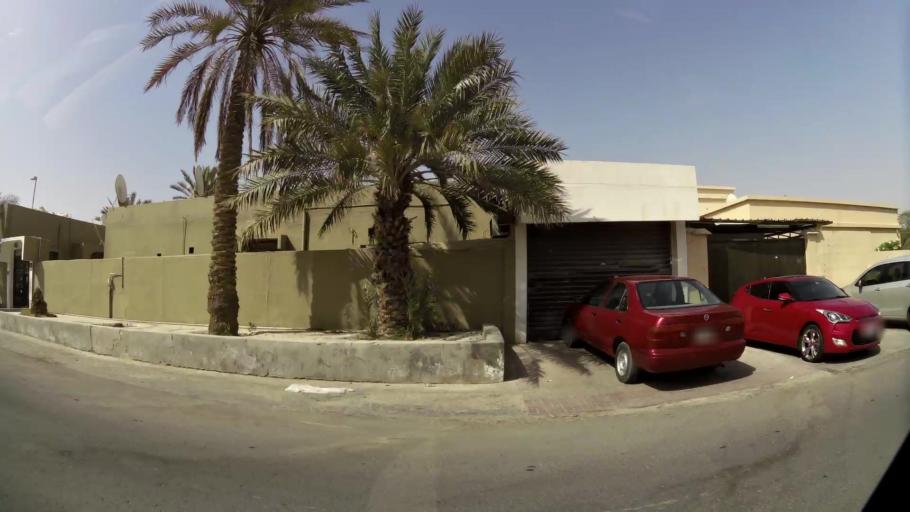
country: AE
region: Dubai
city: Dubai
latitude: 25.1651
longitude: 55.2545
